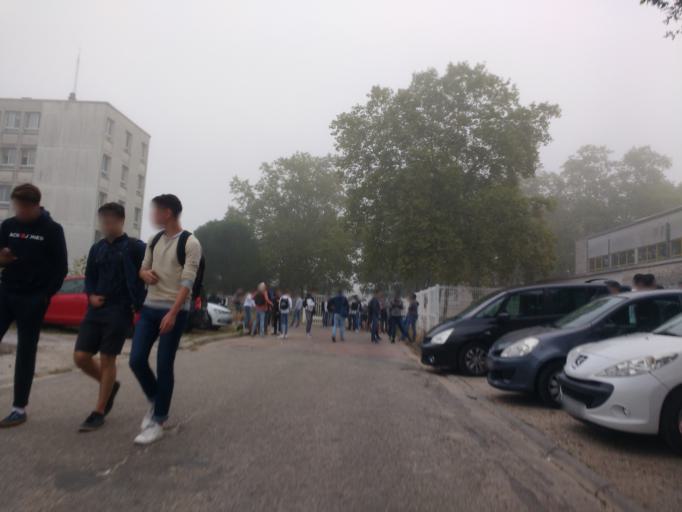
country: FR
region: Aquitaine
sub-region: Departement de la Gironde
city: Talence
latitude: 44.8012
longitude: -0.6028
